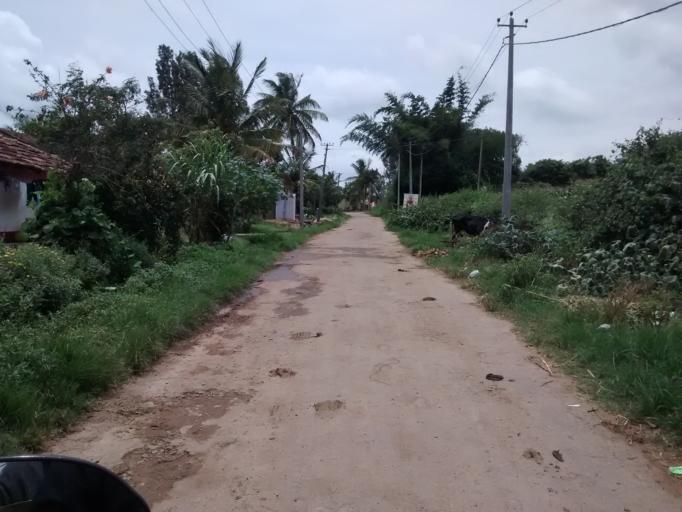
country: IN
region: Karnataka
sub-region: Hassan
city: Hassan
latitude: 12.9092
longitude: 76.1283
